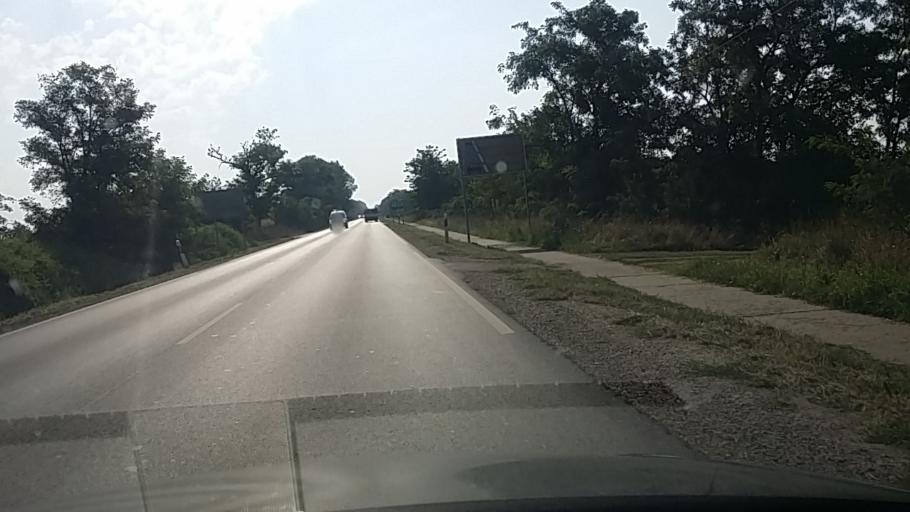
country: HU
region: Bekes
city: Kondoros
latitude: 46.7640
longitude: 20.7801
